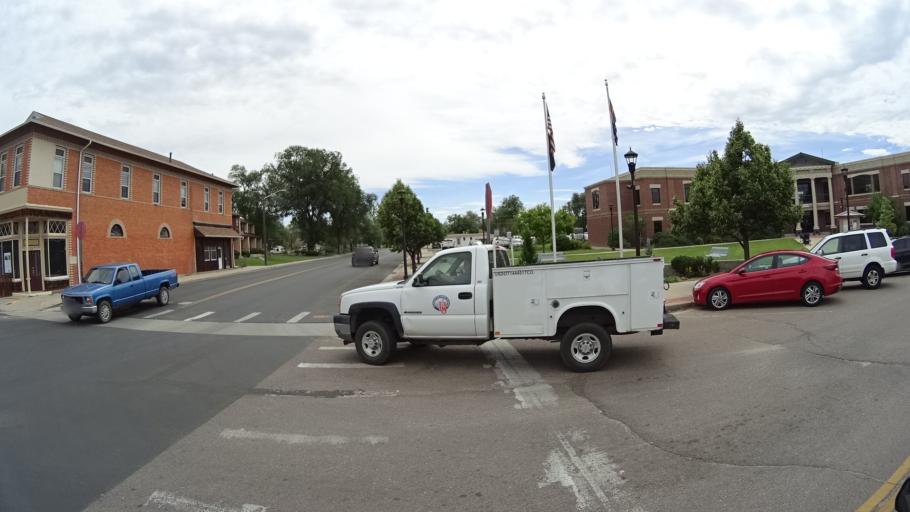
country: US
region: Colorado
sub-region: El Paso County
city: Fountain
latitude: 38.6831
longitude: -104.7007
